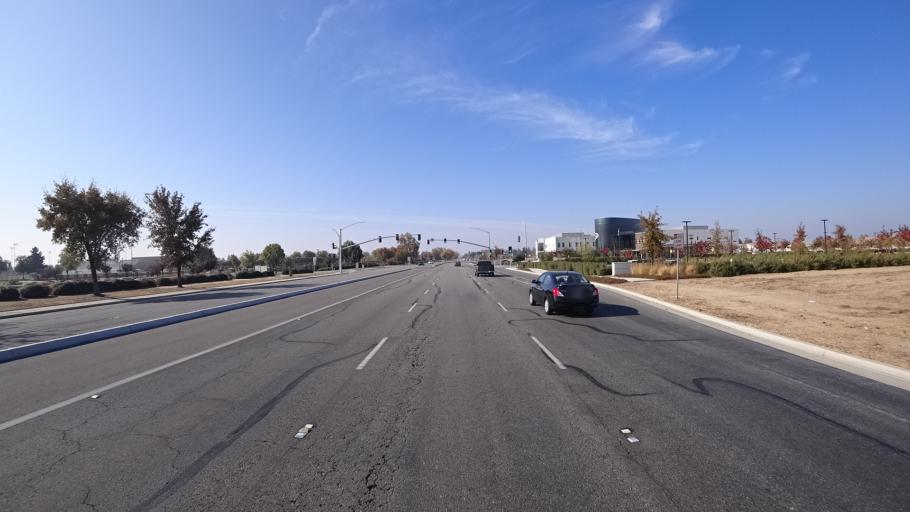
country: US
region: California
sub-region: Kern County
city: Rosedale
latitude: 35.3543
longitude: -119.1397
